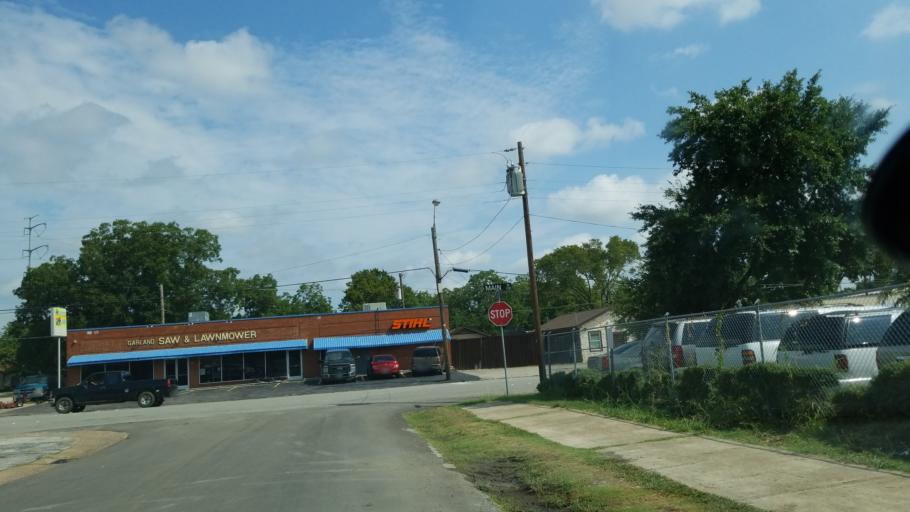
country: US
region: Texas
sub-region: Dallas County
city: Garland
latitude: 32.9124
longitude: -96.6332
